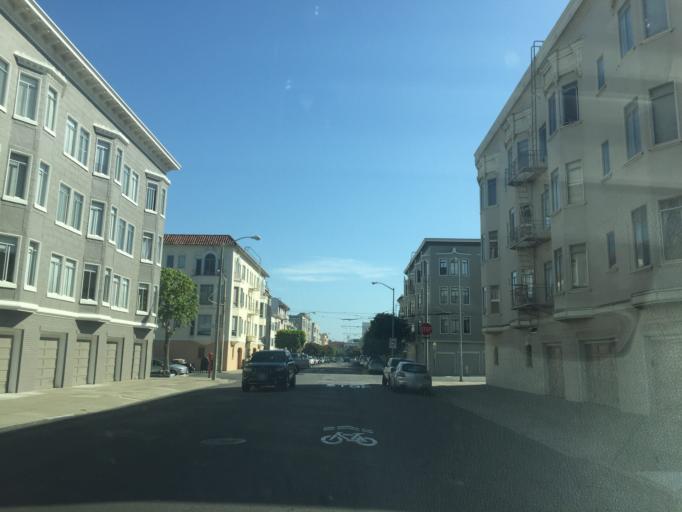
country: US
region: California
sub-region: San Francisco County
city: San Francisco
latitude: 37.8006
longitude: -122.4453
